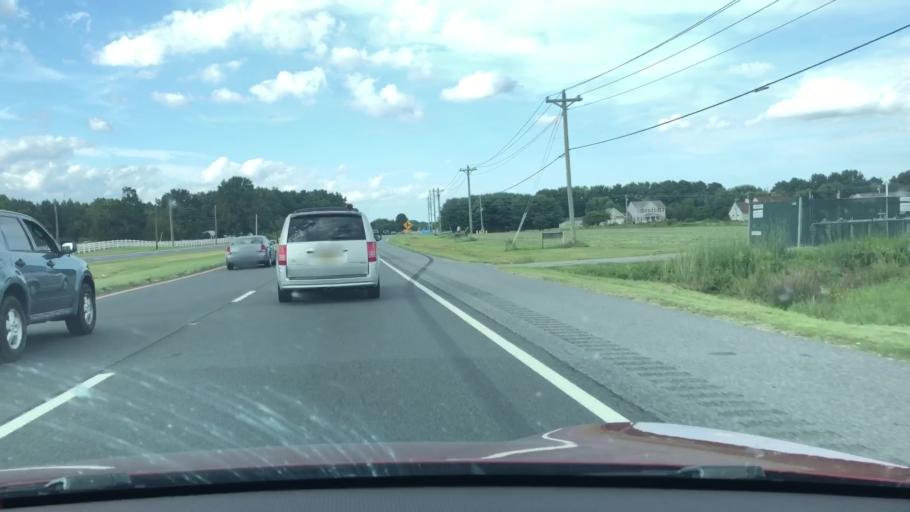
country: US
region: Delaware
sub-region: Sussex County
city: Bridgeville
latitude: 38.8251
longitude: -75.5851
